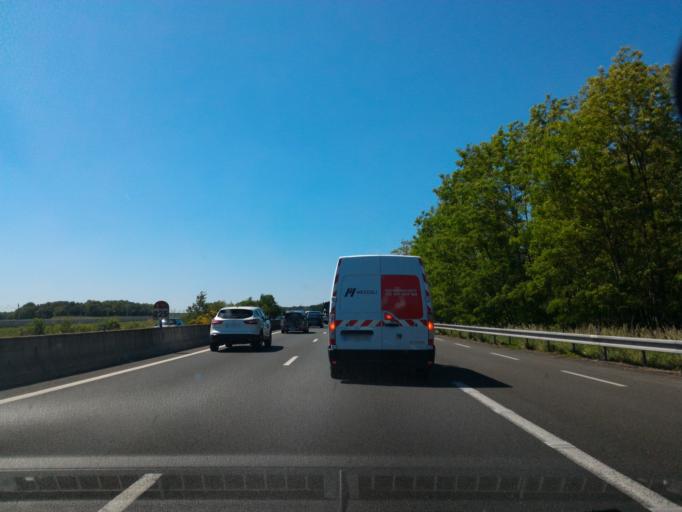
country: FR
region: Centre
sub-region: Departement d'Indre-et-Loire
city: Sorigny
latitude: 47.2407
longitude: 0.6609
